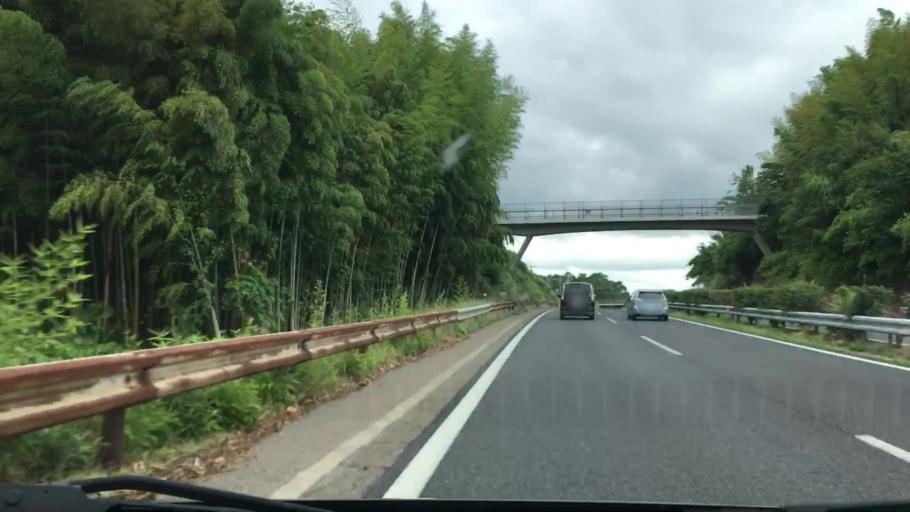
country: JP
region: Okayama
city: Tsuyama
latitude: 35.0714
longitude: 134.0274
